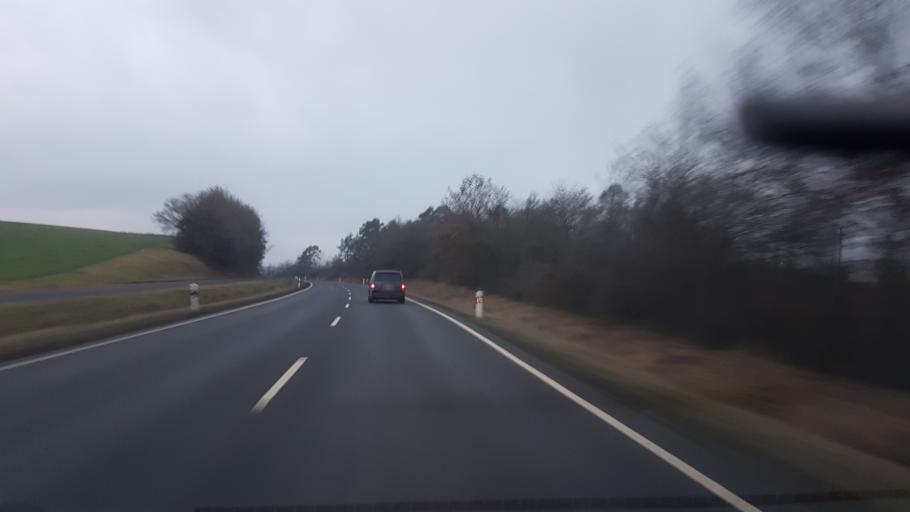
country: DE
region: Bavaria
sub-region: Regierungsbezirk Unterfranken
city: Pfarrweisach
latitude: 50.1372
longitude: 10.7544
